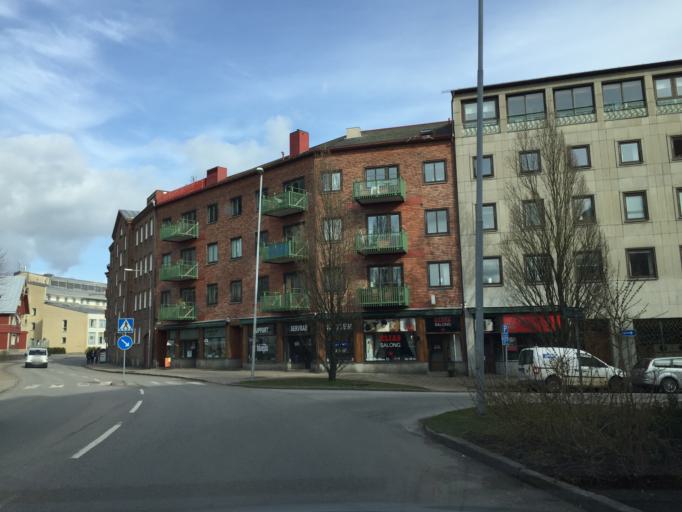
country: SE
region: Vaestra Goetaland
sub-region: Uddevalla Kommun
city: Uddevalla
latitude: 58.3506
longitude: 11.9377
